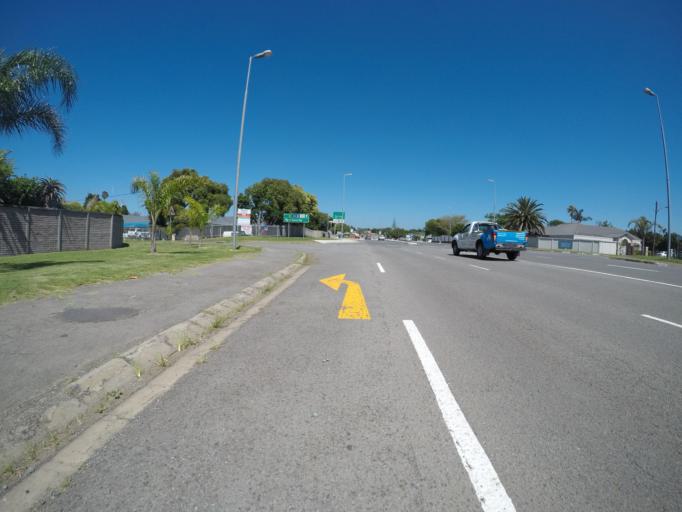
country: ZA
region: Eastern Cape
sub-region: Buffalo City Metropolitan Municipality
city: East London
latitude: -32.9665
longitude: 27.9430
